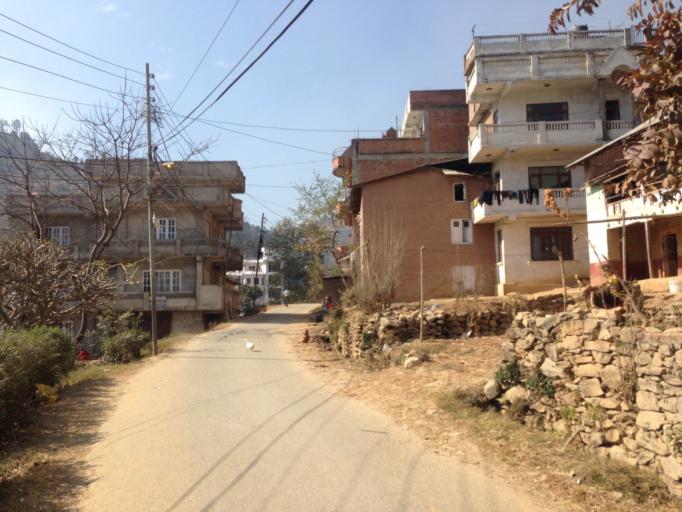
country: NP
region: Central Region
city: Kirtipur
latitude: 27.7289
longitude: 85.2666
